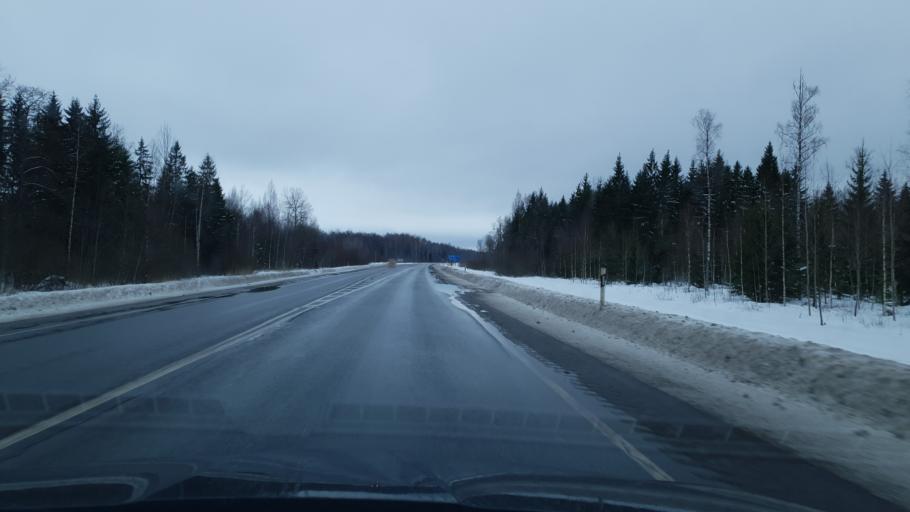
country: EE
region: Tartu
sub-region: Puhja vald
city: Puhja
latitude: 58.5135
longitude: 26.3219
